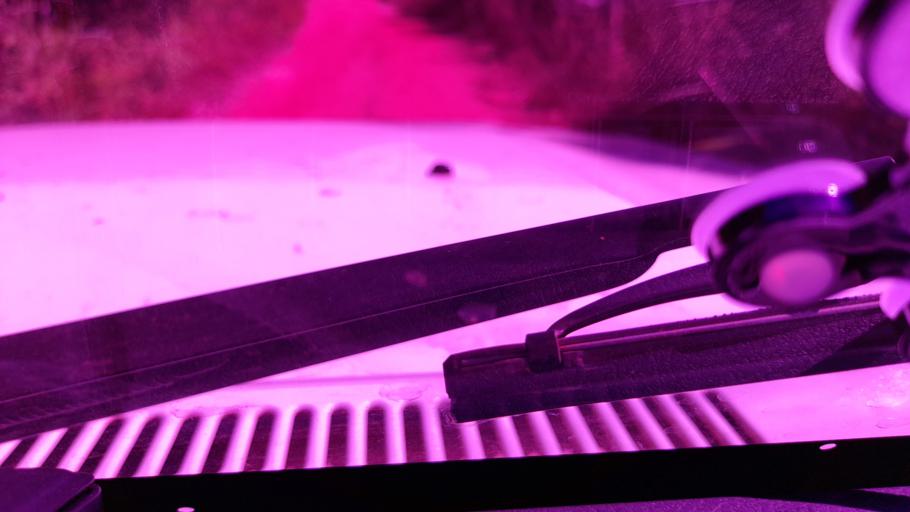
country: SN
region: Ziguinchor
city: Adeane
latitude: 12.4092
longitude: -15.7865
